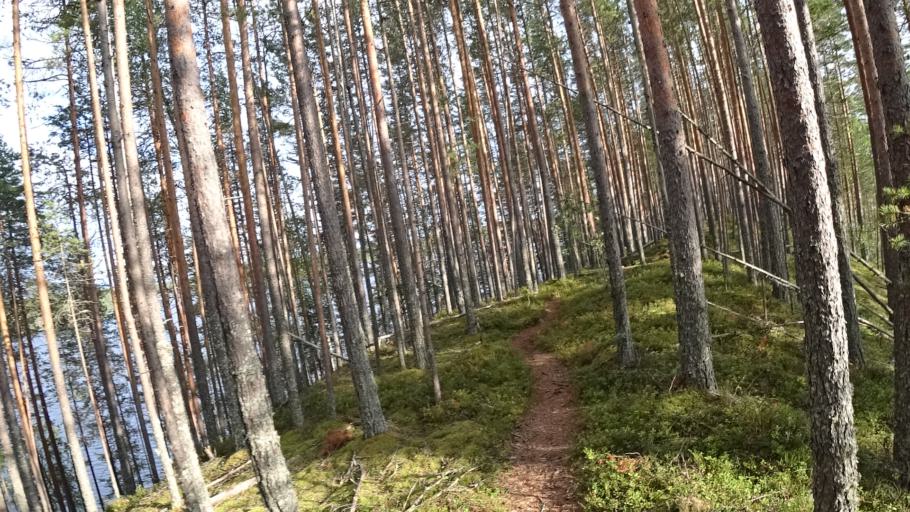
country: FI
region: North Karelia
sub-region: Joensuu
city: Ilomantsi
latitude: 62.5698
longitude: 31.1794
